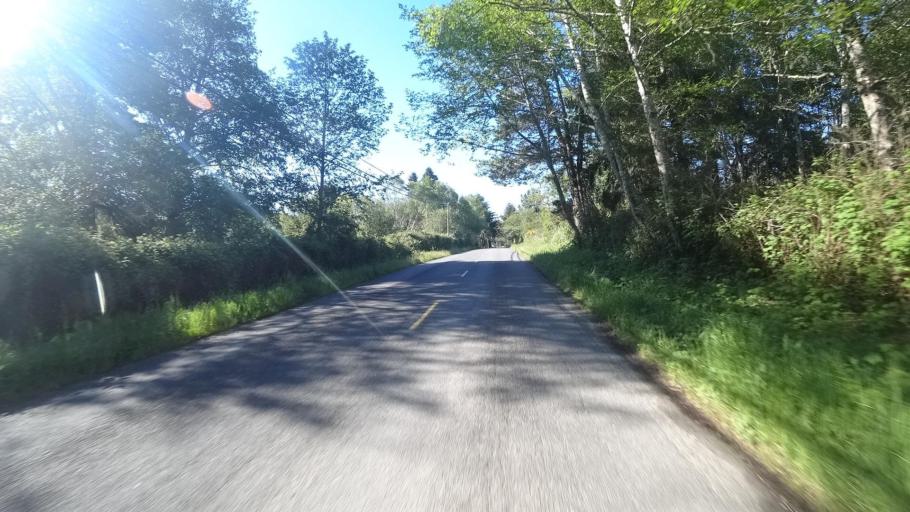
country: US
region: California
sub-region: Humboldt County
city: McKinleyville
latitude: 40.9668
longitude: -124.0959
